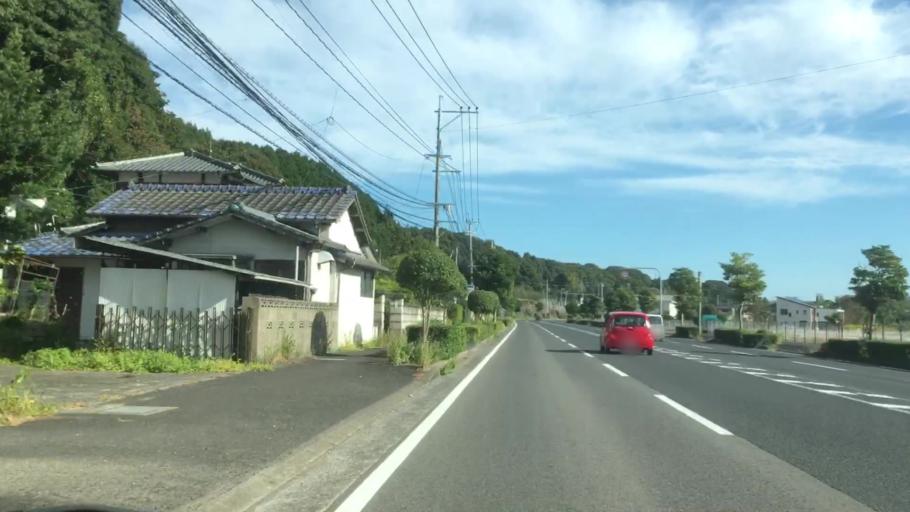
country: JP
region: Nagasaki
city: Sasebo
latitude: 33.1109
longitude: 129.7863
